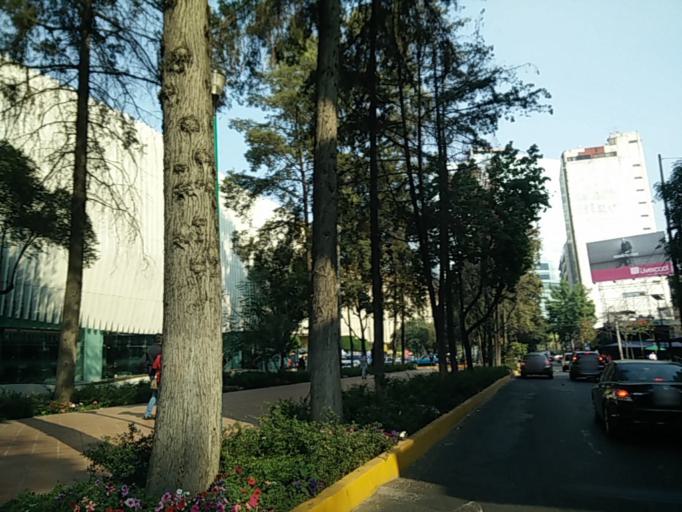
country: MX
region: Mexico City
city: Miguel Hidalgo
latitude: 19.4331
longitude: -99.1841
